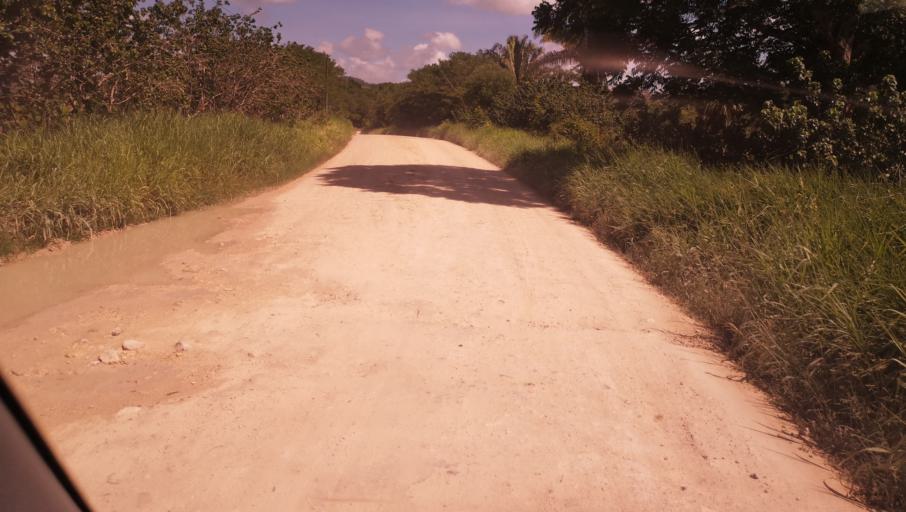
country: GT
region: Peten
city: Melchor de Mencos
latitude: 17.0157
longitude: -89.2434
